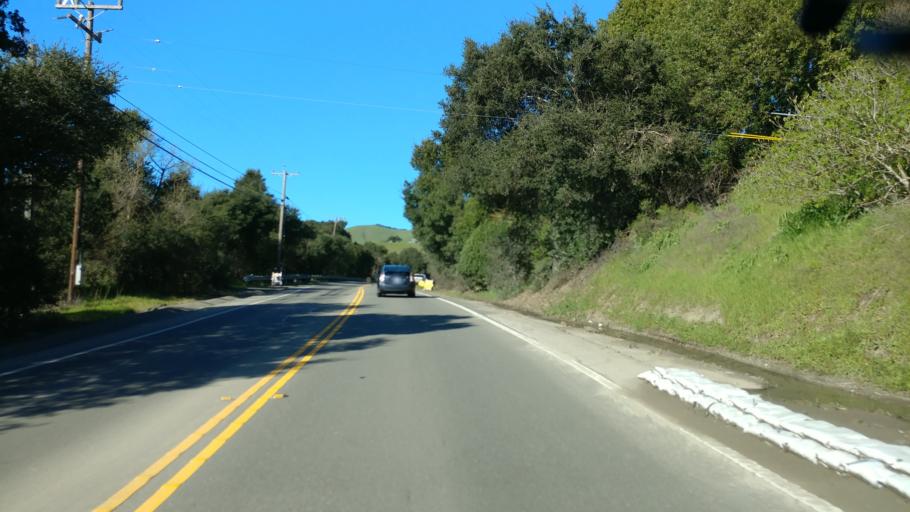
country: US
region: California
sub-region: Contra Costa County
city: San Ramon
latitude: 37.7577
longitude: -122.0288
